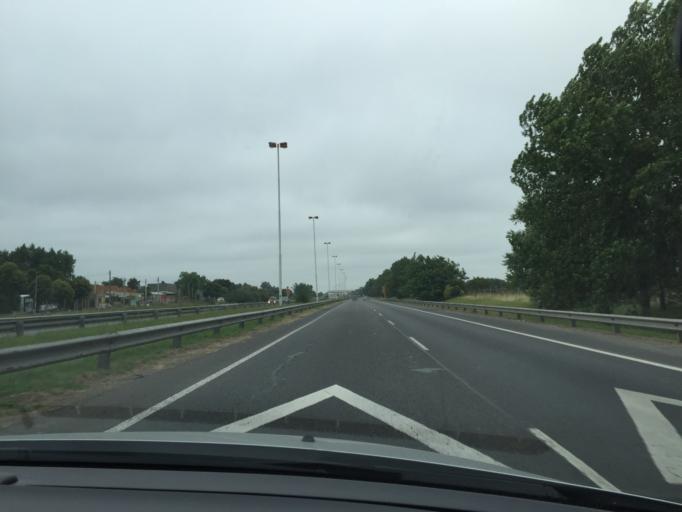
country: AR
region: Buenos Aires
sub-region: Partido de Ezeiza
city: Ezeiza
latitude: -34.8438
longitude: -58.5323
